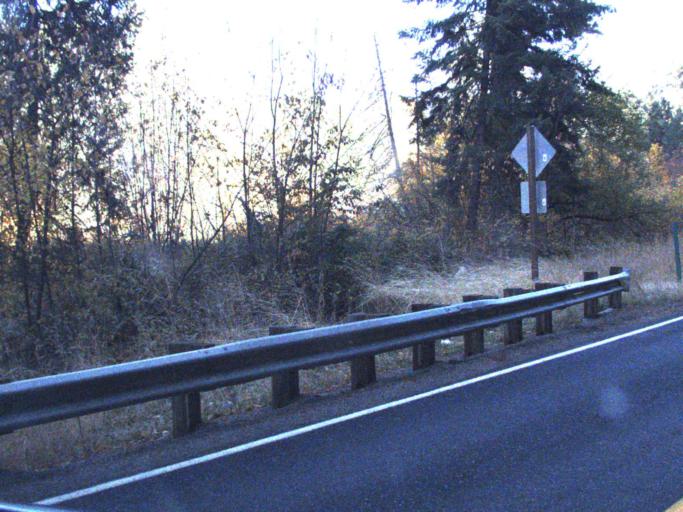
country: US
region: Washington
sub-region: Stevens County
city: Kettle Falls
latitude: 48.6621
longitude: -118.0723
